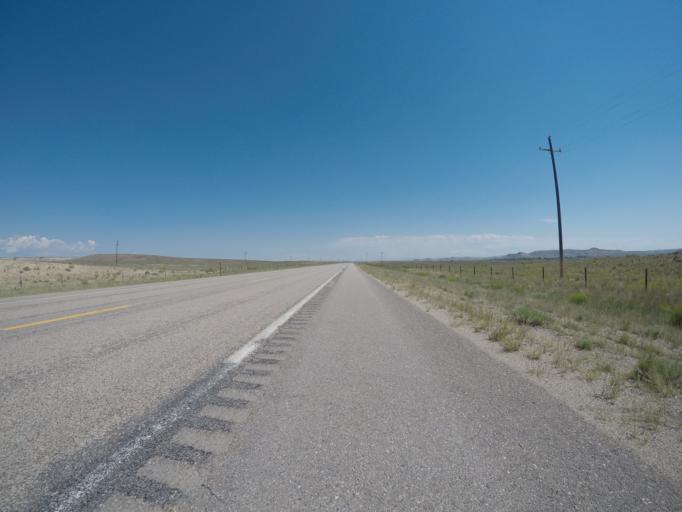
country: US
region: Wyoming
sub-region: Sublette County
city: Marbleton
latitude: 42.4002
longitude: -110.1231
